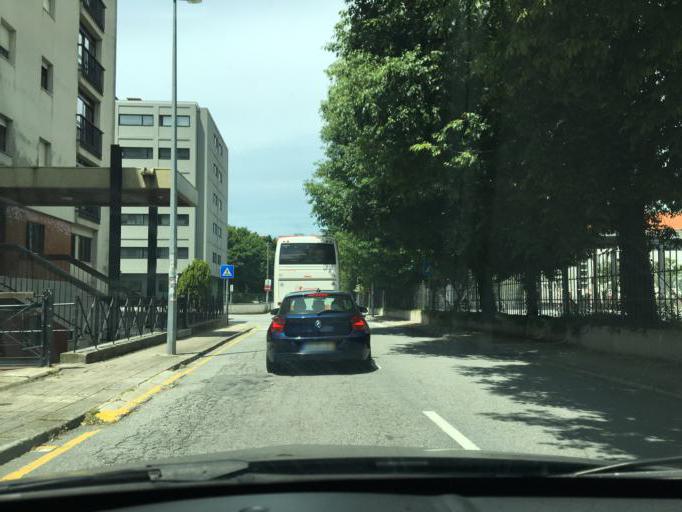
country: PT
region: Porto
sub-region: Porto
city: Porto
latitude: 41.1657
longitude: -8.6079
